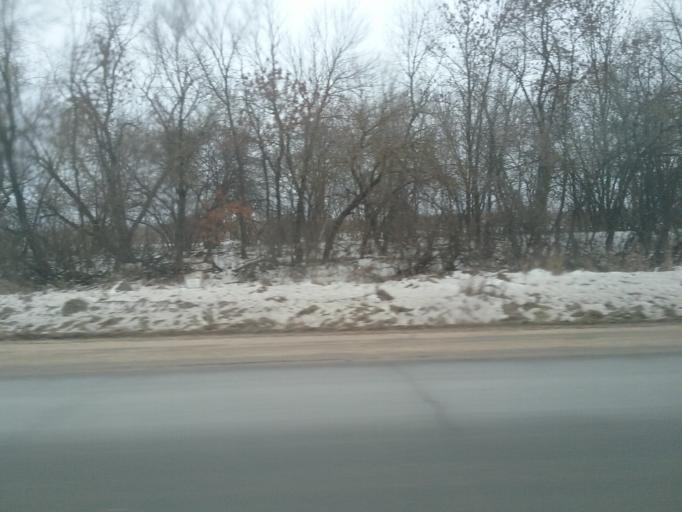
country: RU
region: Tula
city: Bolokhovo
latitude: 54.1052
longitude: 37.7590
